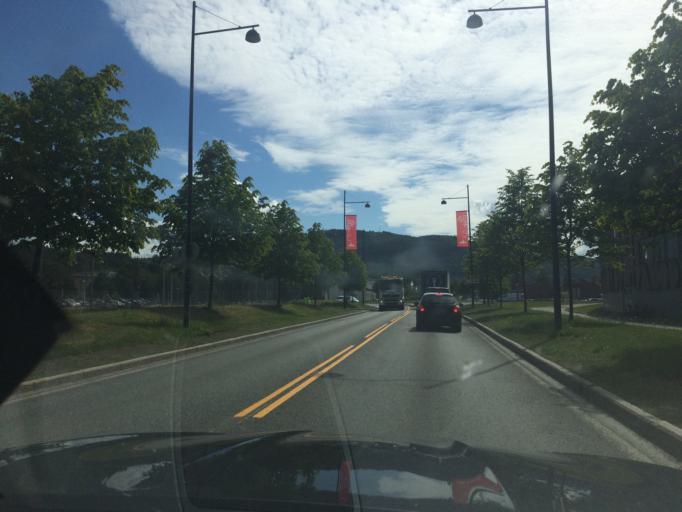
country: NO
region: Nord-Trondelag
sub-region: Steinkjer
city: Steinkjer
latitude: 64.0116
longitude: 11.4946
